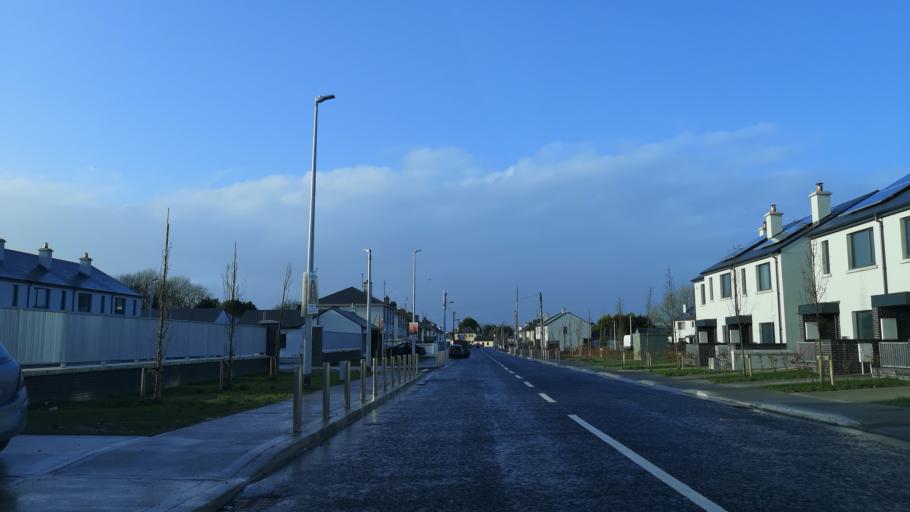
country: IE
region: Connaught
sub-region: County Galway
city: Tuam
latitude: 53.5098
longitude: -8.8575
